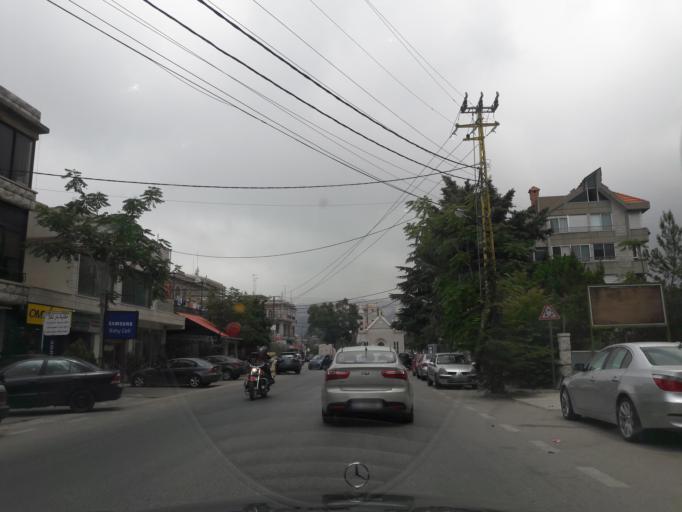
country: LB
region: Mont-Liban
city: Bhamdoun el Mhatta
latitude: 33.9123
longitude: 35.7481
